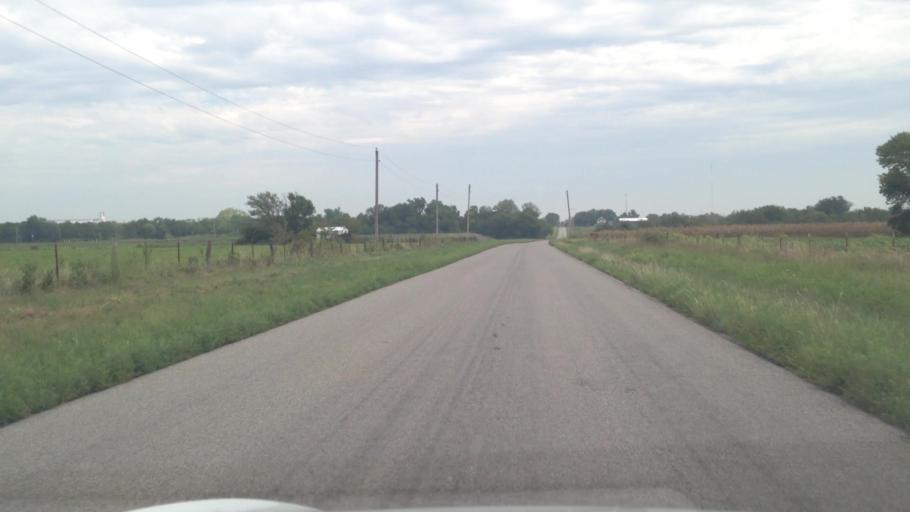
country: US
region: Kansas
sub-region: Crawford County
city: Girard
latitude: 37.4994
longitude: -94.8625
